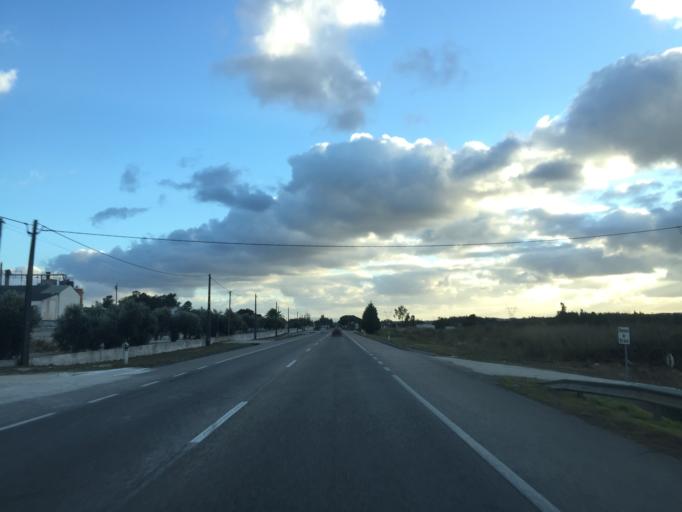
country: PT
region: Leiria
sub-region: Alcobaca
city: Turquel
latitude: 39.4503
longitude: -8.9498
